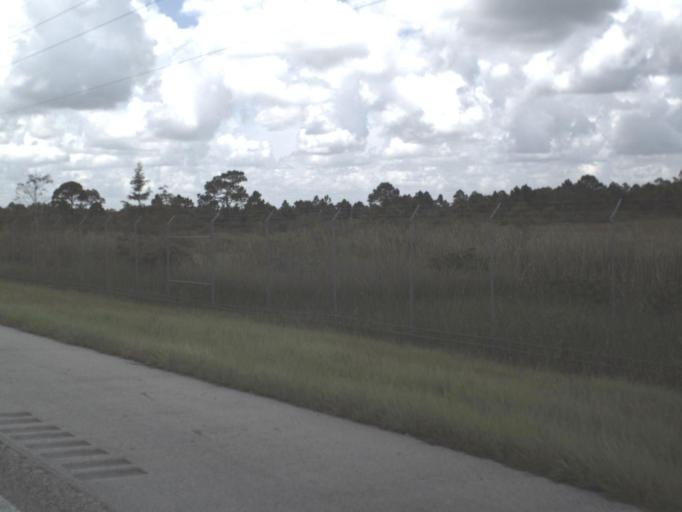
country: US
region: Florida
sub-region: Collier County
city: Immokalee
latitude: 26.1712
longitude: -80.9576
